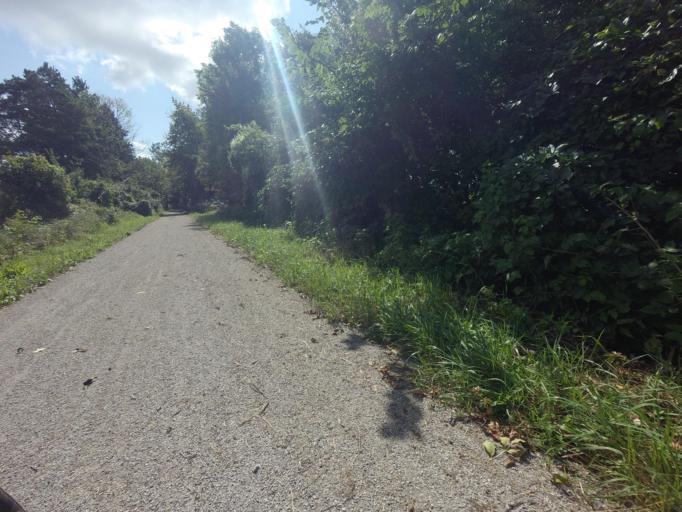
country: CA
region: Ontario
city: Huron East
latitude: 43.6793
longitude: -81.2973
